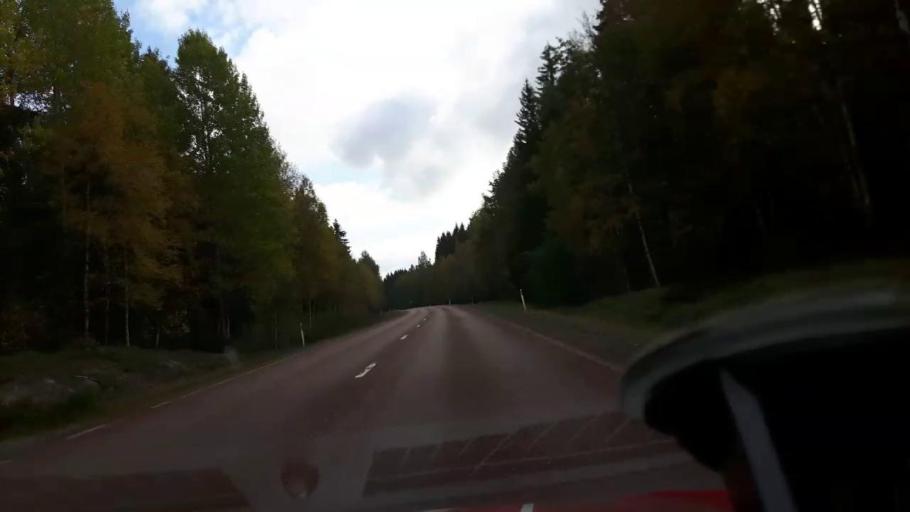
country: SE
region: Gaevleborg
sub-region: Ljusdals Kommun
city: Jaervsoe
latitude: 61.6396
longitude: 16.2366
